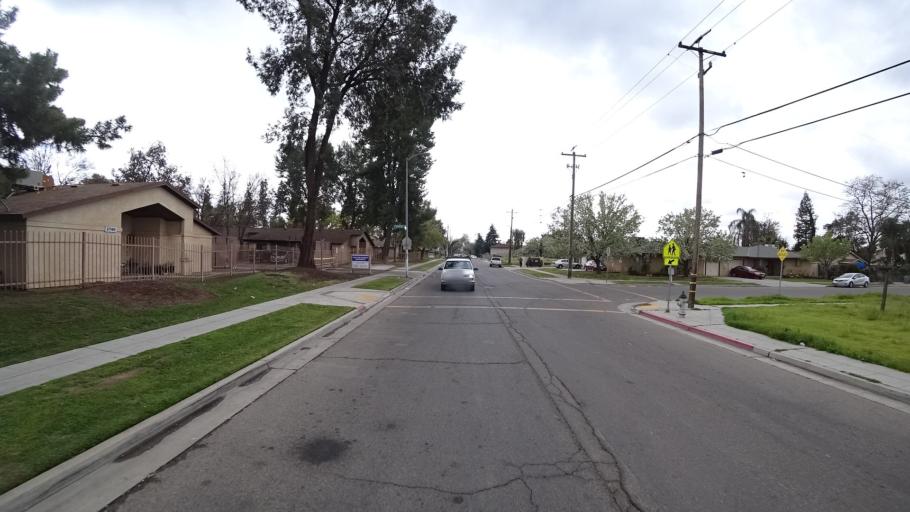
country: US
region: California
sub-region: Fresno County
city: West Park
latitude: 36.7857
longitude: -119.8400
